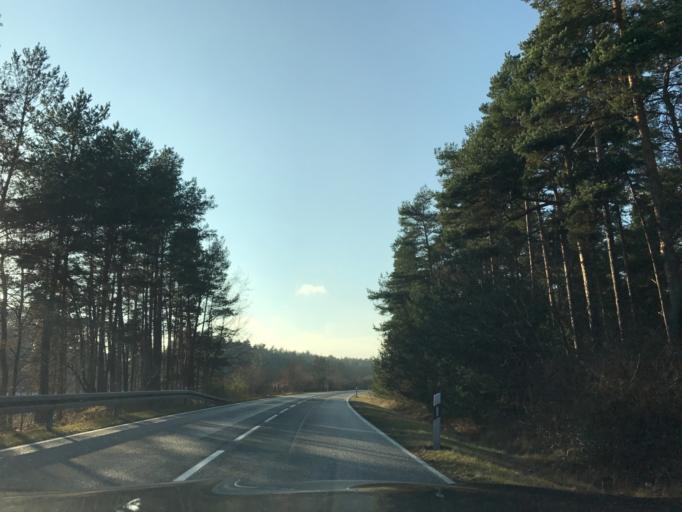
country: DE
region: Brandenburg
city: Wenzlow
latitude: 52.2797
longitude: 12.4400
